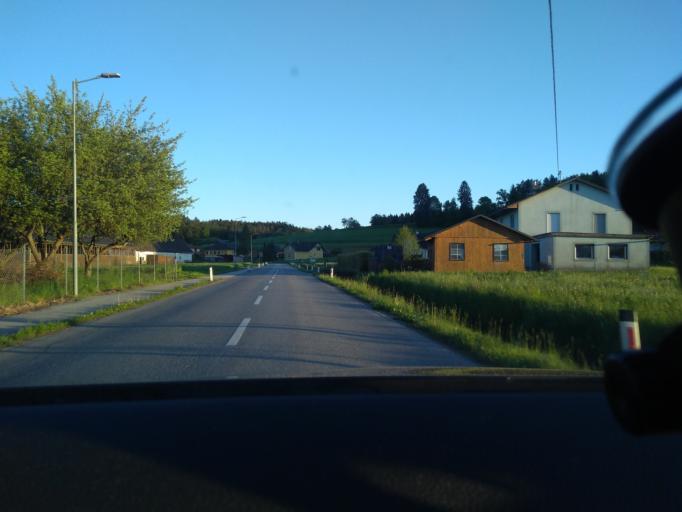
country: AT
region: Styria
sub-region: Politischer Bezirk Voitsberg
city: Mooskirchen
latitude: 46.9776
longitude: 15.2825
